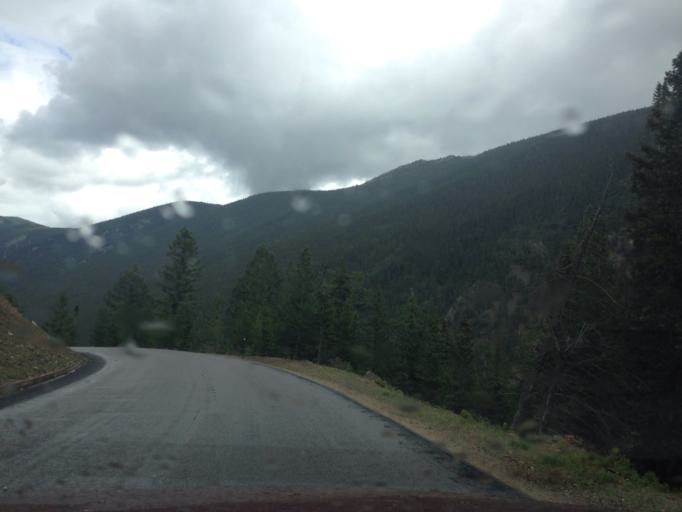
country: US
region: Colorado
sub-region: Clear Creek County
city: Georgetown
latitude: 39.6780
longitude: -105.7035
